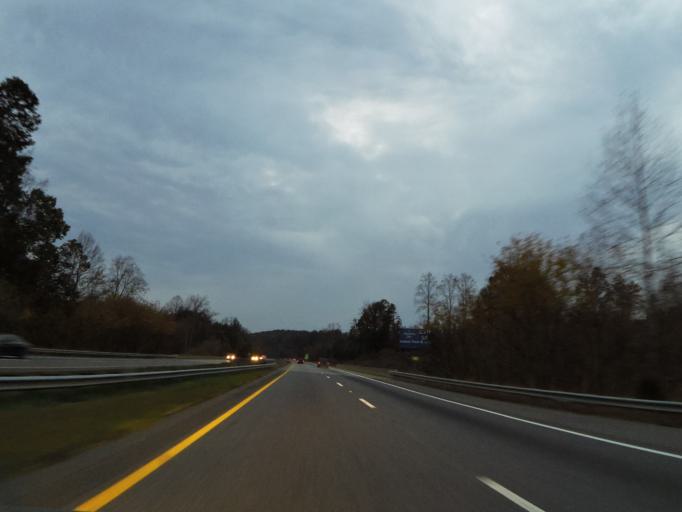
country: US
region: North Carolina
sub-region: McDowell County
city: Marion
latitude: 35.6831
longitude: -81.9308
